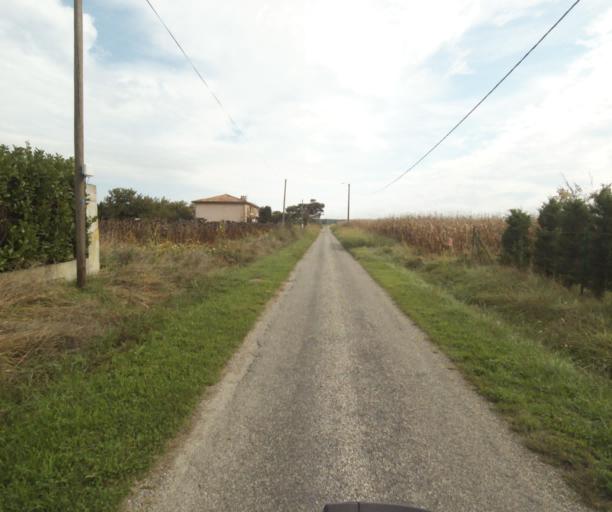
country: FR
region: Midi-Pyrenees
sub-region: Departement du Tarn-et-Garonne
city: Finhan
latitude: 43.9196
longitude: 1.2319
